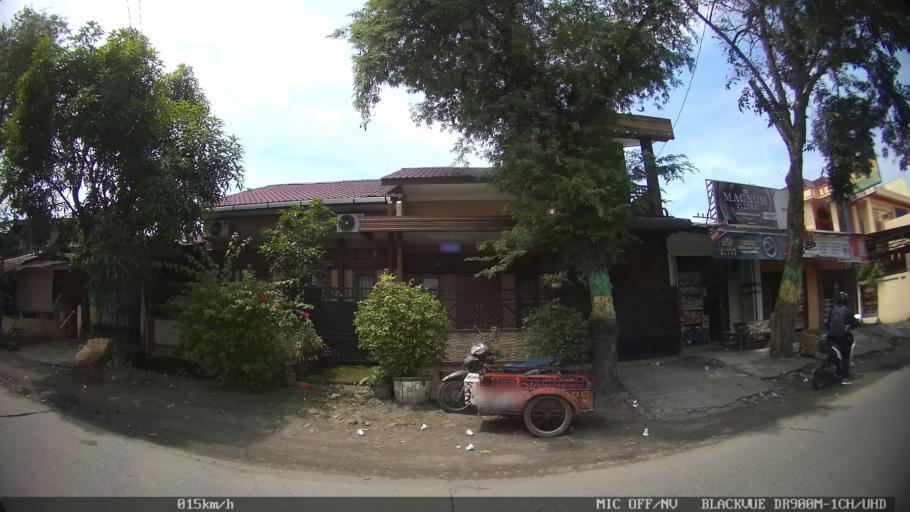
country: ID
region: North Sumatra
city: Labuhan Deli
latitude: 3.6573
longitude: 98.6684
